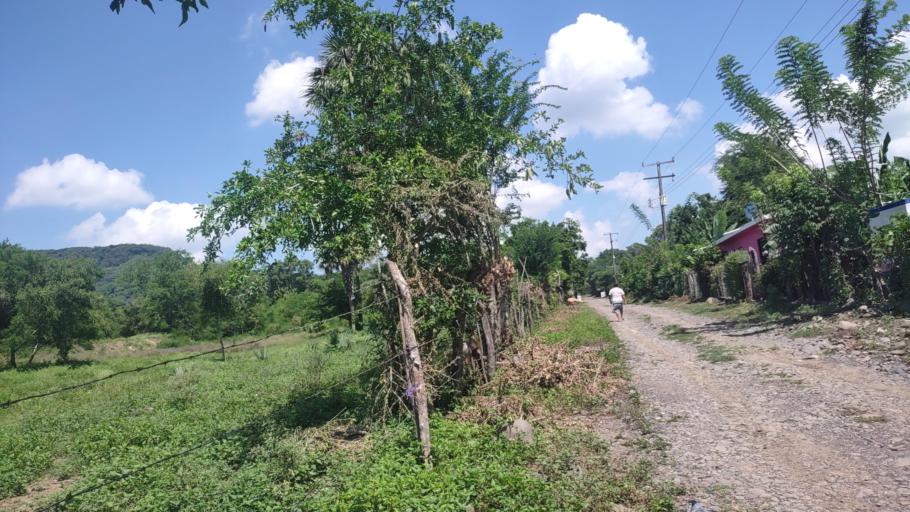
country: MX
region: Veracruz
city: Los Altos
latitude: 21.4315
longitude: -97.7915
